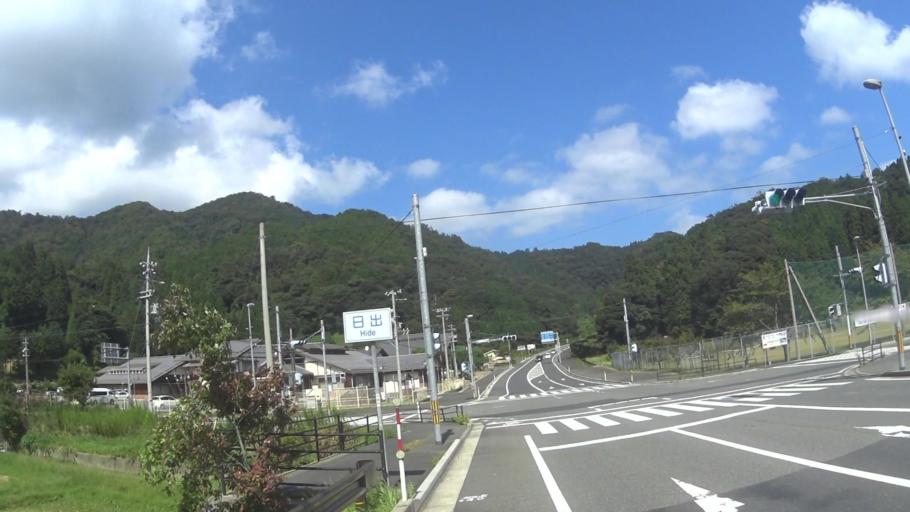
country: JP
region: Kyoto
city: Miyazu
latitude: 35.6740
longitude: 135.2726
